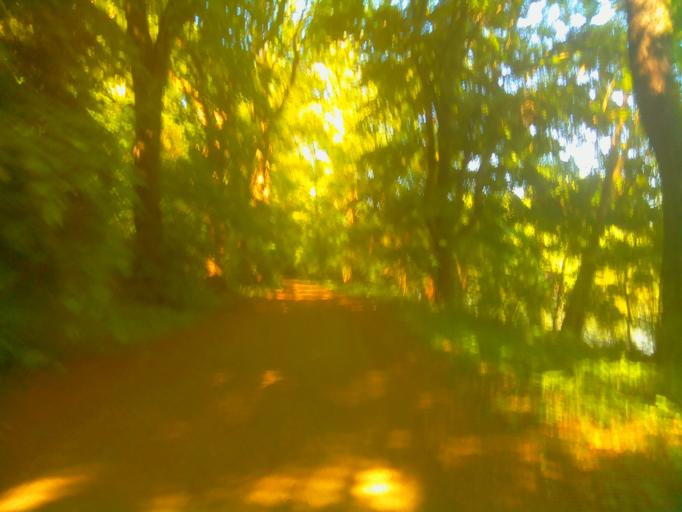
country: DE
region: Thuringia
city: Rudolstadt
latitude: 50.7159
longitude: 11.3281
